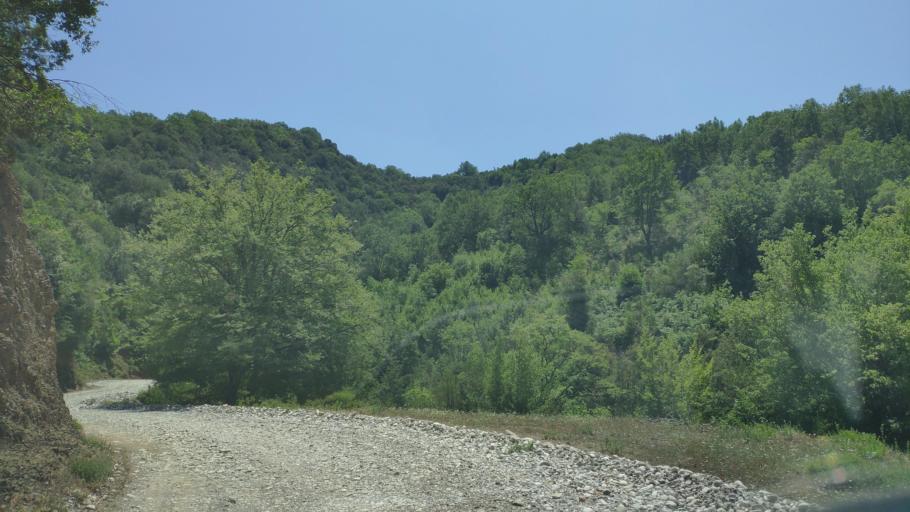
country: GR
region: Epirus
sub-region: Nomos Artas
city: Ano Kalentini
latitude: 39.1778
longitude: 21.3618
